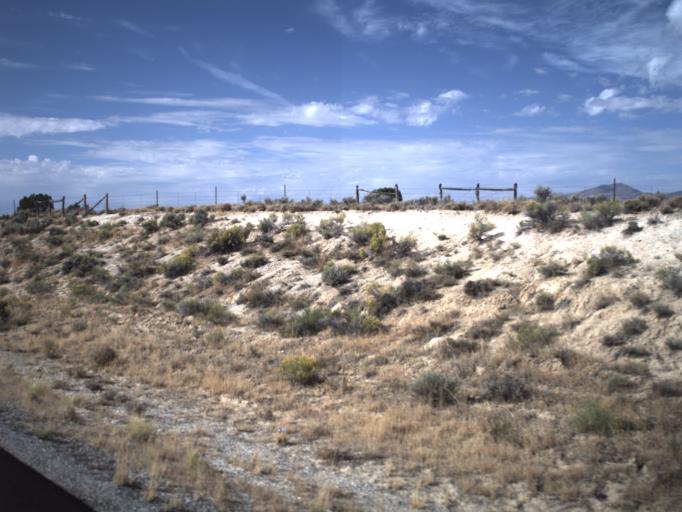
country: US
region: Idaho
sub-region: Cassia County
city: Burley
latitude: 41.7143
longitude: -113.5288
